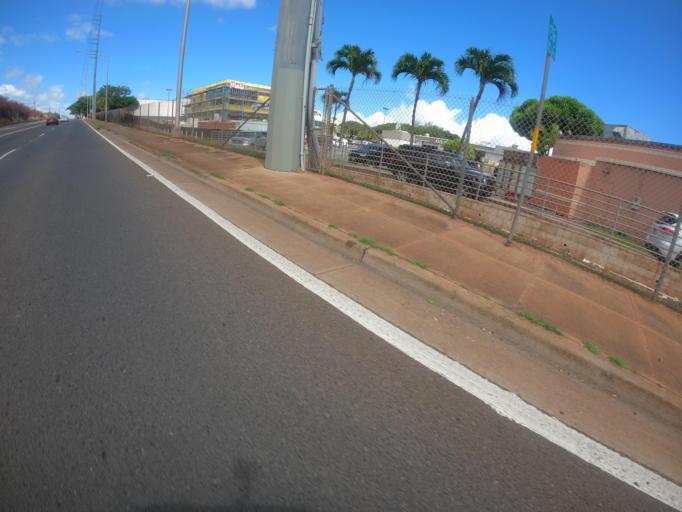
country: US
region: Hawaii
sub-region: Honolulu County
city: Royal Kunia
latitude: 21.3886
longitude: -158.0345
